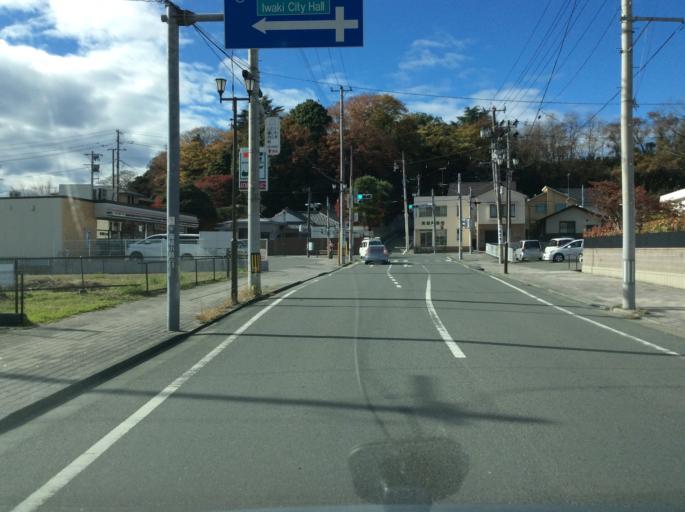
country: JP
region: Fukushima
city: Iwaki
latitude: 37.0571
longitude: 140.8883
